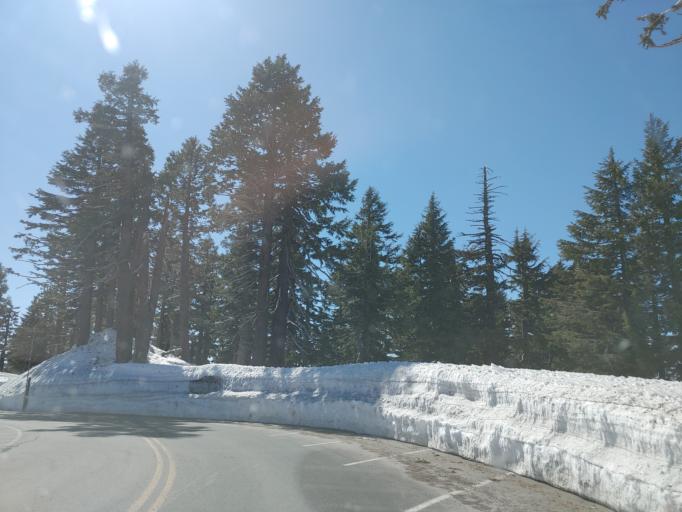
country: US
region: Oregon
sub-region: Jackson County
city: Shady Cove
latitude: 42.9115
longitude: -122.1475
